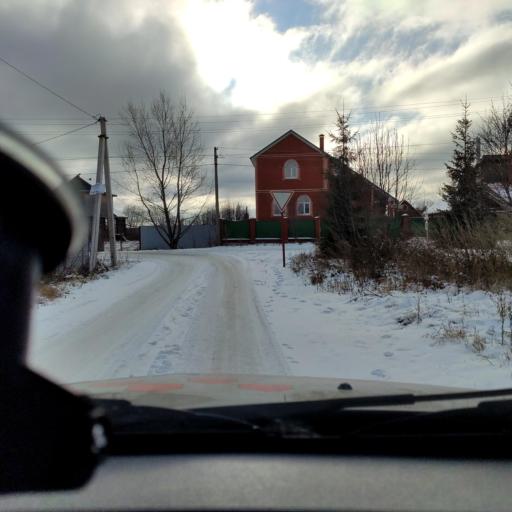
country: RU
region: Bashkortostan
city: Avdon
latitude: 54.7851
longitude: 55.7213
